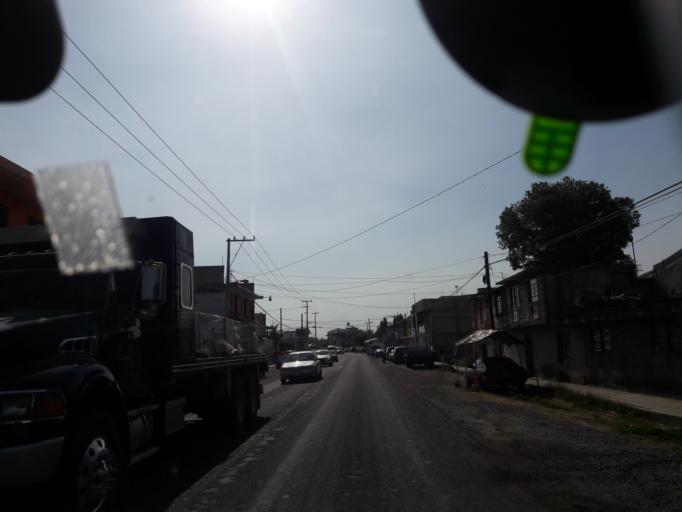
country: MX
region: Tlaxcala
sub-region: Ixtacuixtla de Mariano Matamoros
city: Villa Mariano Matamoros
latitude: 19.3085
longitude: -98.3767
